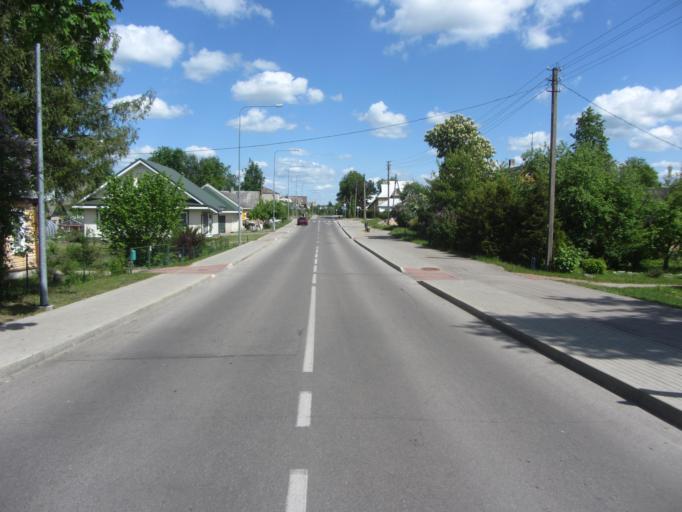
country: LT
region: Utenos apskritis
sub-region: Utena
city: Utena
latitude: 55.5003
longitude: 25.5878
